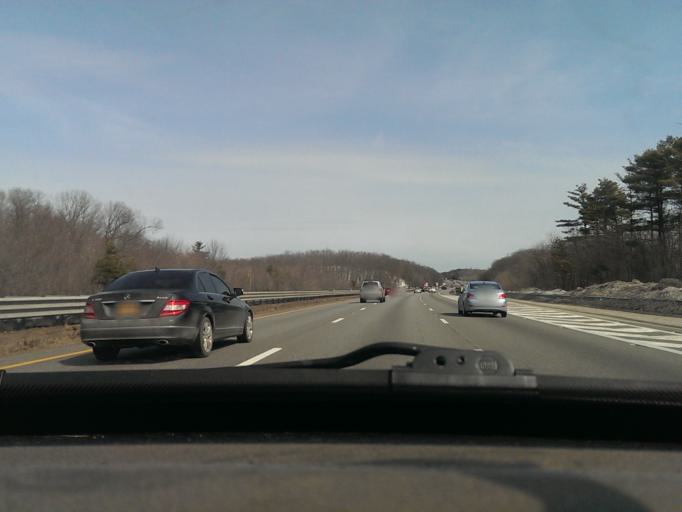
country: US
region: Massachusetts
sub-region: Worcester County
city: Charlton
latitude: 42.1737
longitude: -71.9243
